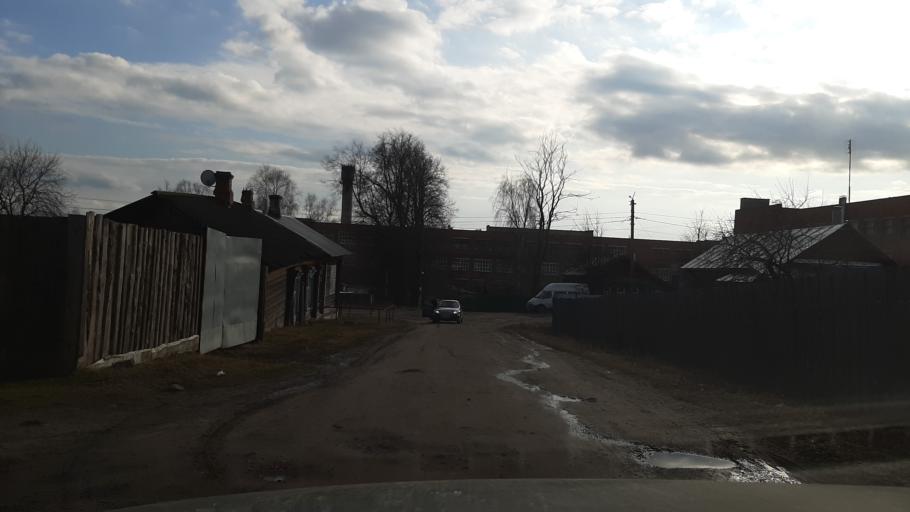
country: RU
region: Ivanovo
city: Teykovo
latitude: 56.8532
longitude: 40.5579
